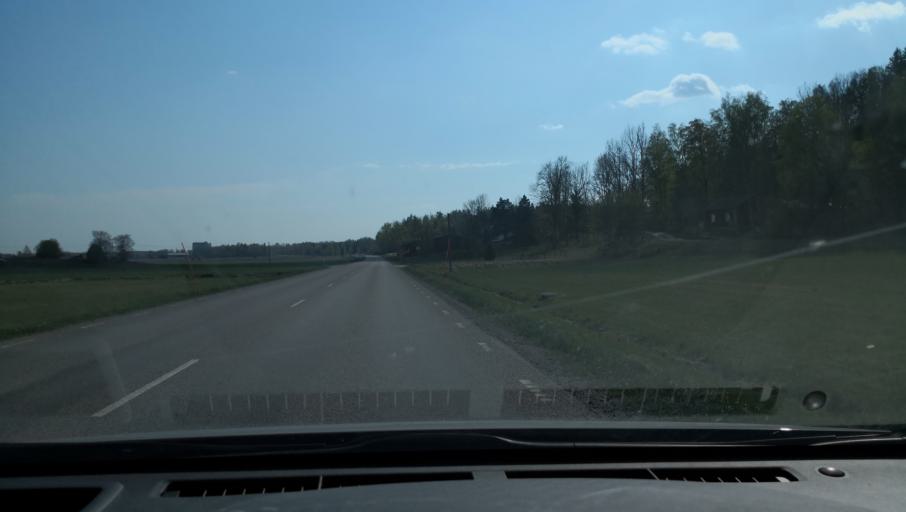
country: SE
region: Vaestmanland
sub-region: Sala Kommun
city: Sala
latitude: 59.9588
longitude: 16.6192
